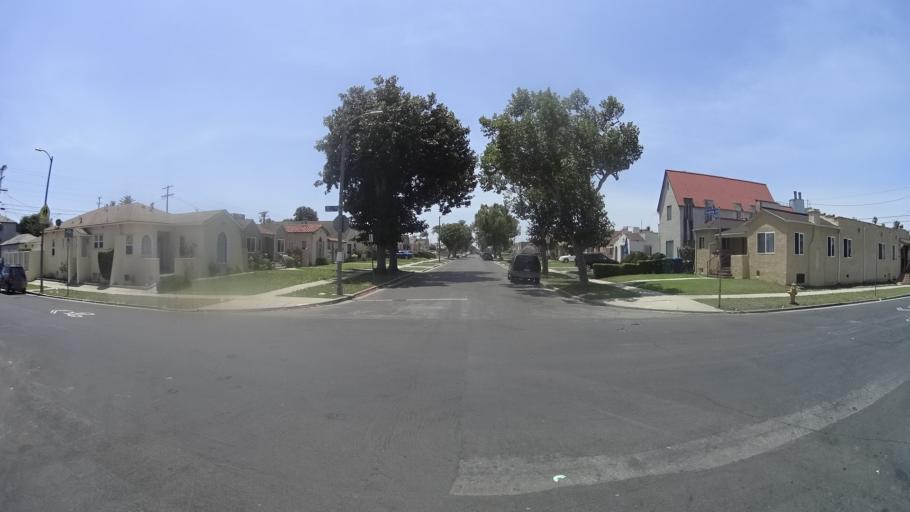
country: US
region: California
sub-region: Los Angeles County
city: Westmont
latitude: 33.9710
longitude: -118.3014
